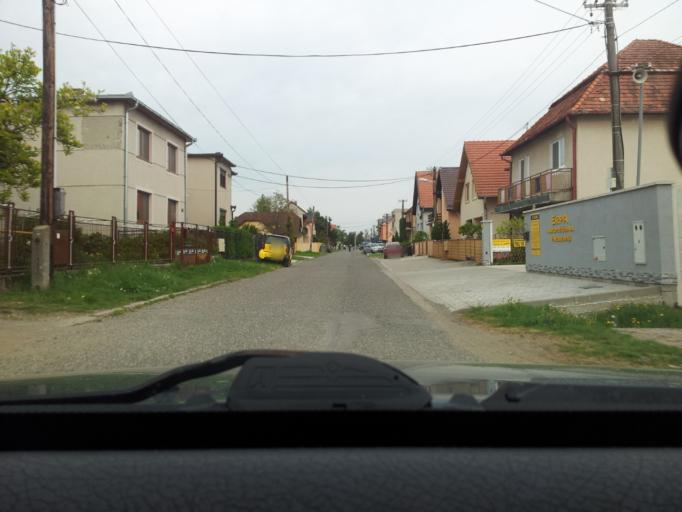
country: SK
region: Nitriansky
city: Levice
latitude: 48.2672
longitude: 18.5894
